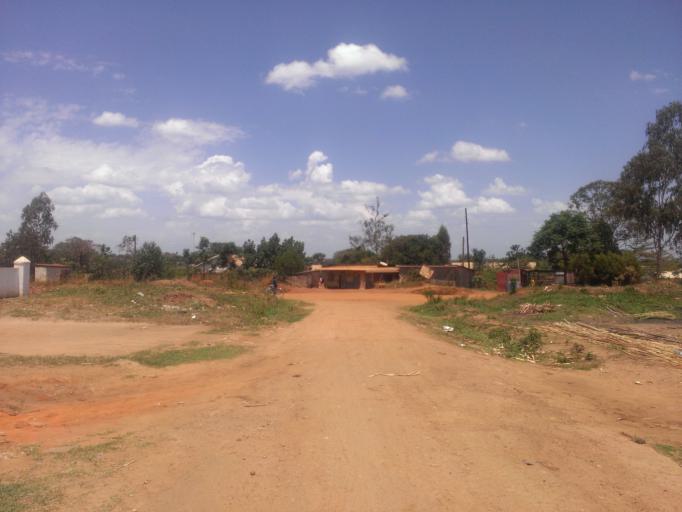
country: UG
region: Northern Region
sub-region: Gulu District
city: Gulu
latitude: 2.7834
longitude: 32.2943
